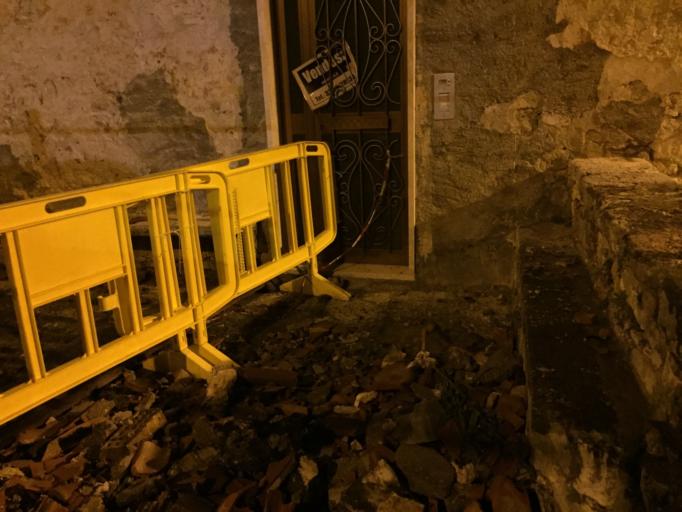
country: IT
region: The Marches
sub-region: Provincia di Ascoli Piceno
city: Acquasanta Terme
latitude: 42.7697
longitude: 13.4106
